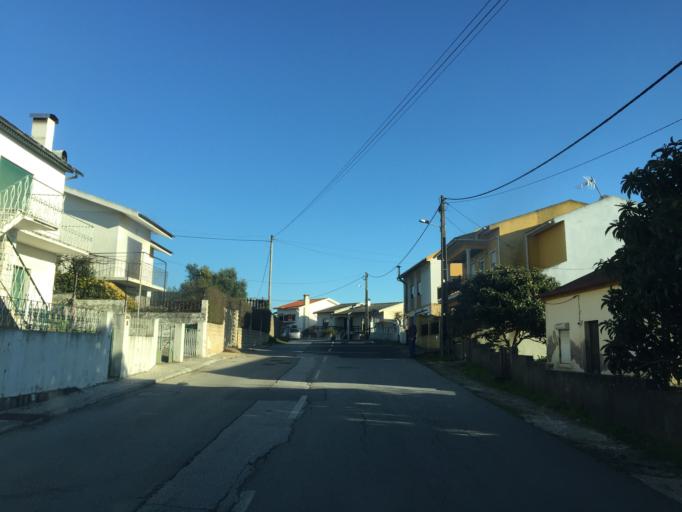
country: PT
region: Coimbra
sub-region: Figueira da Foz
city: Tavarede
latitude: 40.1651
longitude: -8.8341
